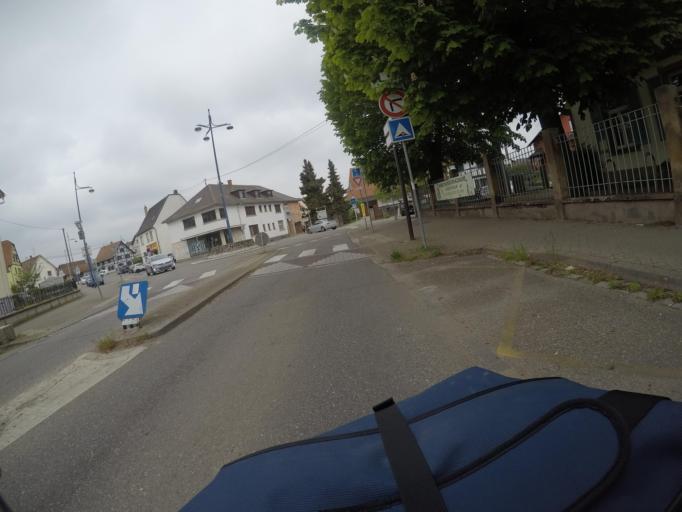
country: FR
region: Alsace
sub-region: Departement du Bas-Rhin
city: La Wantzenau
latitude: 48.6596
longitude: 7.8252
